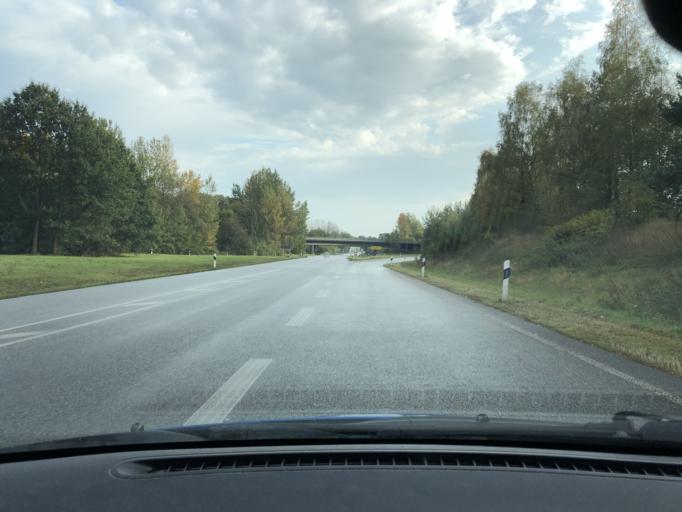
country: DE
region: Schleswig-Holstein
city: Grande
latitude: 53.5905
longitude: 10.3915
